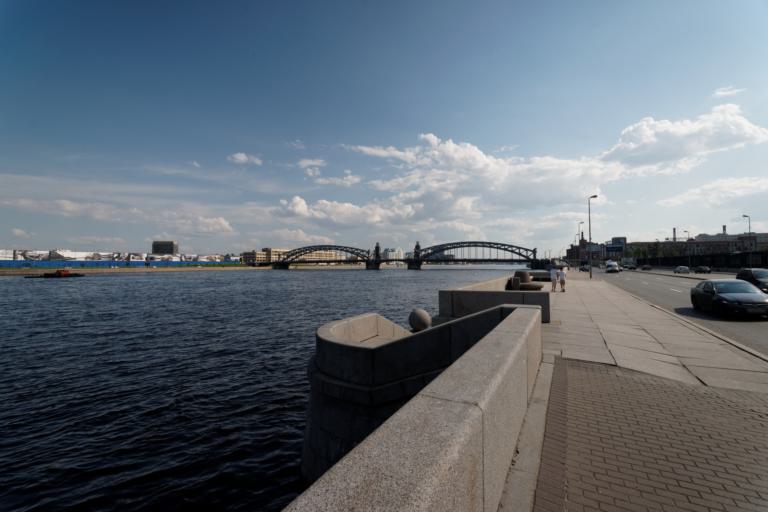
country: RU
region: Leningrad
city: Finlyandskiy
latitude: 59.9464
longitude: 30.3994
